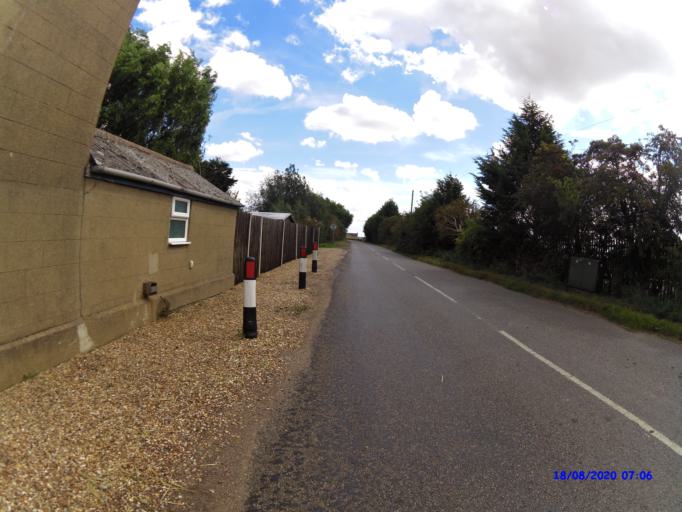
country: GB
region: England
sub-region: Cambridgeshire
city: Whittlesey
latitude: 52.5453
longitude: -0.1135
